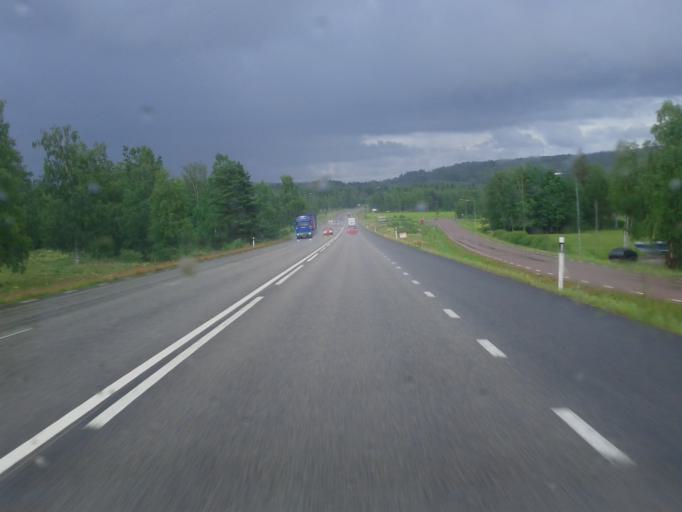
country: SE
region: Dalarna
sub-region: Rattviks Kommun
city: Vikarbyn
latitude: 60.9133
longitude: 15.0309
